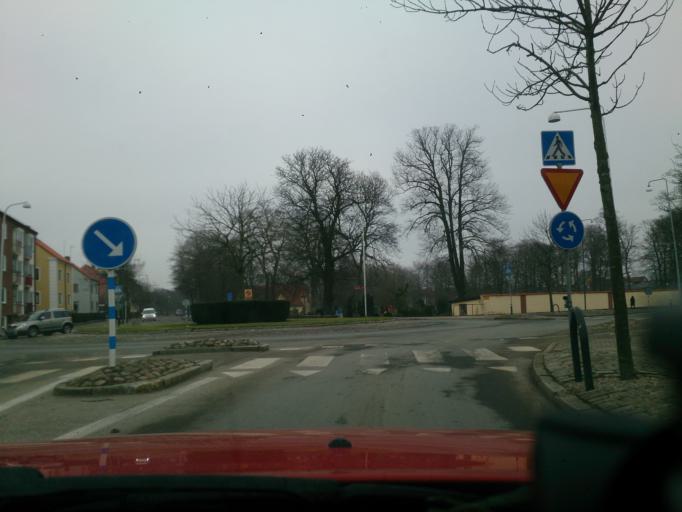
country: SE
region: Skane
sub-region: Ystads Kommun
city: Ystad
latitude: 55.4281
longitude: 13.8085
